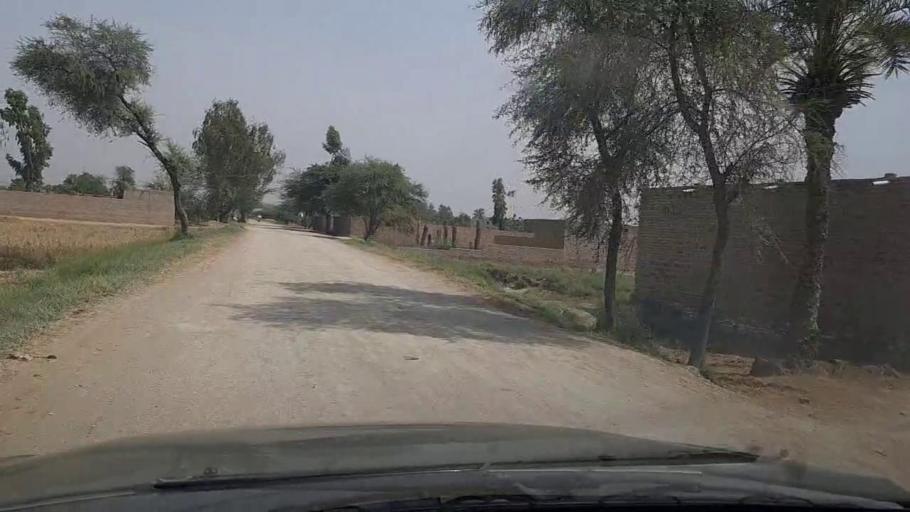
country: PK
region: Sindh
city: Shikarpur
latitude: 27.9257
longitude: 68.6672
